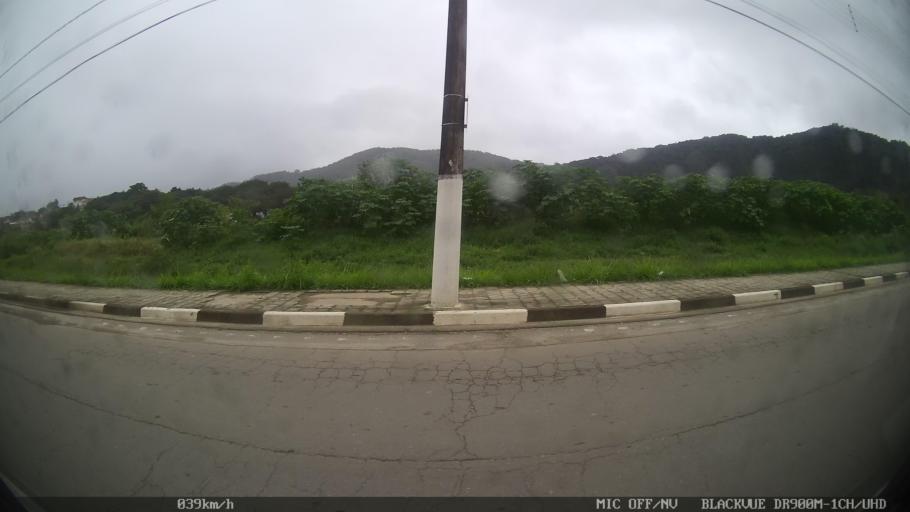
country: BR
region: Sao Paulo
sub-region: Juquia
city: Juquia
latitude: -24.3169
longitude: -47.6335
